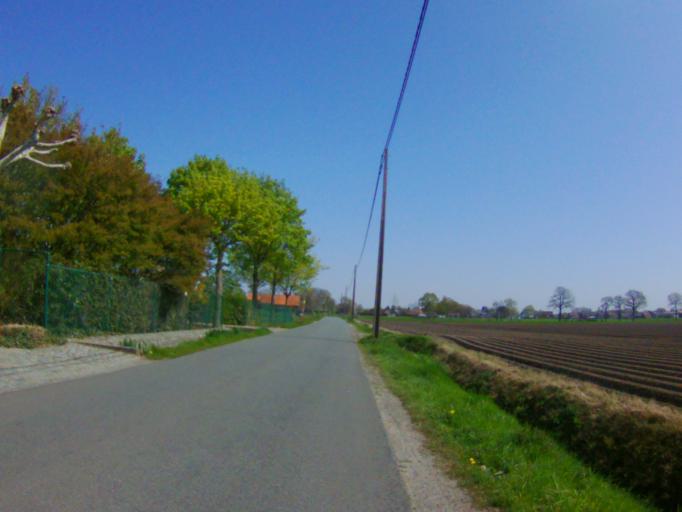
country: BE
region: Flanders
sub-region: Provincie Antwerpen
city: Brecht
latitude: 51.3376
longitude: 4.6452
